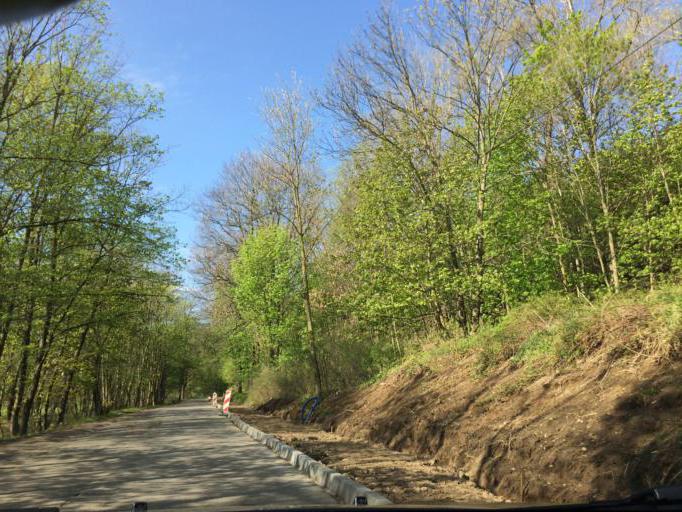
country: PL
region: Lower Silesian Voivodeship
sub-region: Powiat dzierzoniowski
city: Pieszyce
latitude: 50.6889
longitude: 16.5513
